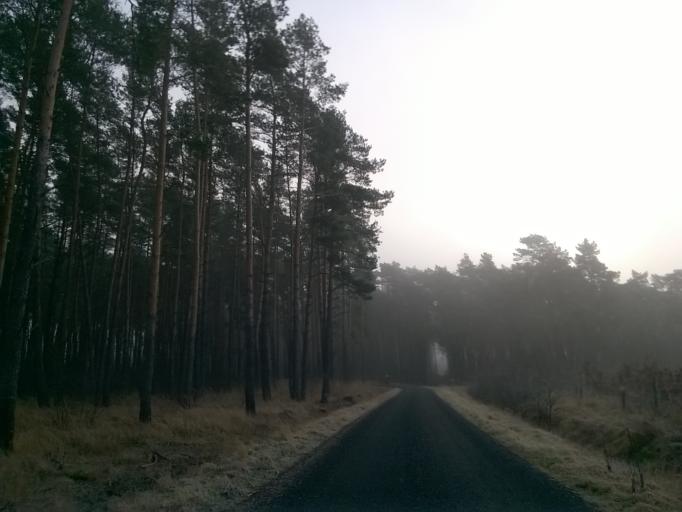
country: PL
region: Kujawsko-Pomorskie
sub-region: Powiat nakielski
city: Kcynia
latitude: 53.0547
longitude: 17.4474
